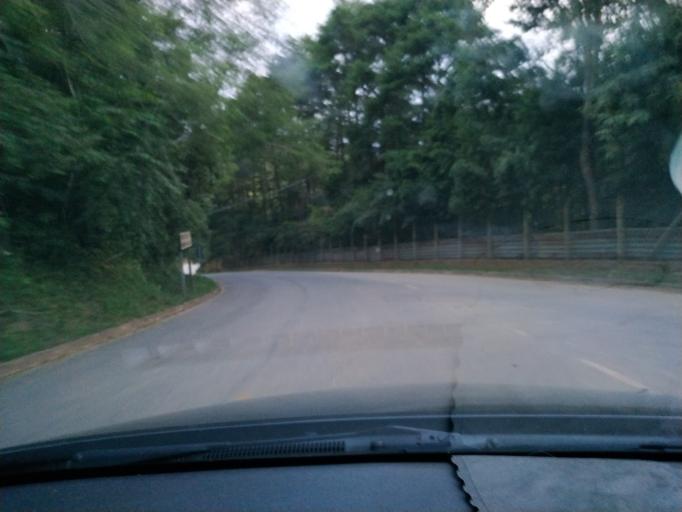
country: BR
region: Sao Paulo
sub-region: Campos Do Jordao
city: Campos do Jordao
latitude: -22.8180
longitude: -45.6639
